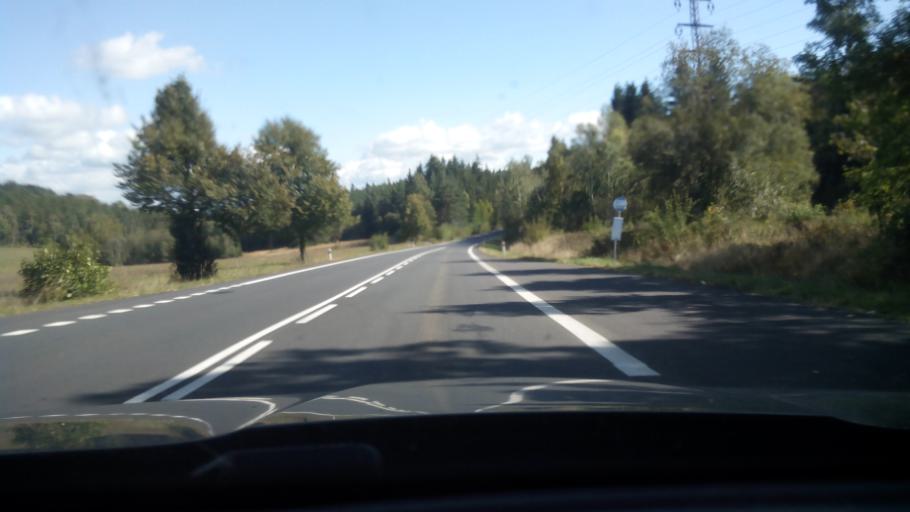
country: CZ
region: Jihocesky
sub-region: Okres Prachatice
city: Zdikov
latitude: 49.0674
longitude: 13.7240
